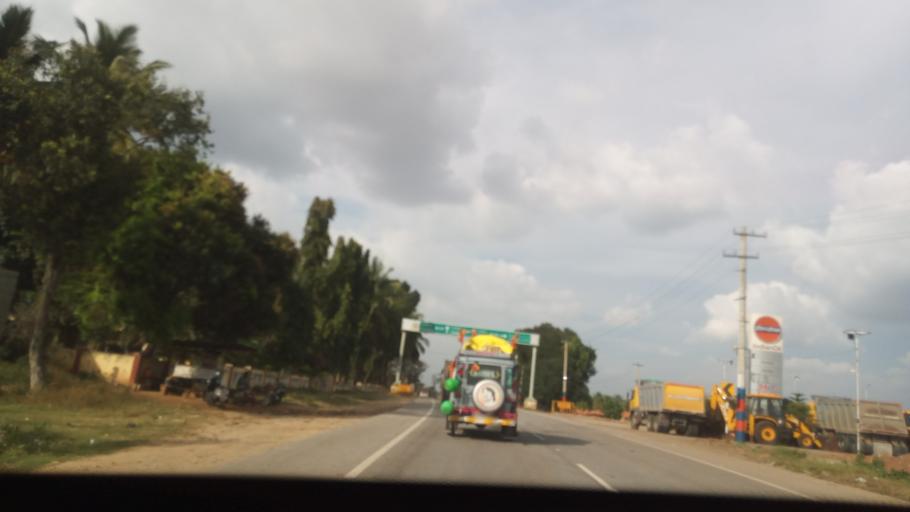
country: IN
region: Karnataka
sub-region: Tumkur
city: Kunigal
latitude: 12.8405
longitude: 77.0351
